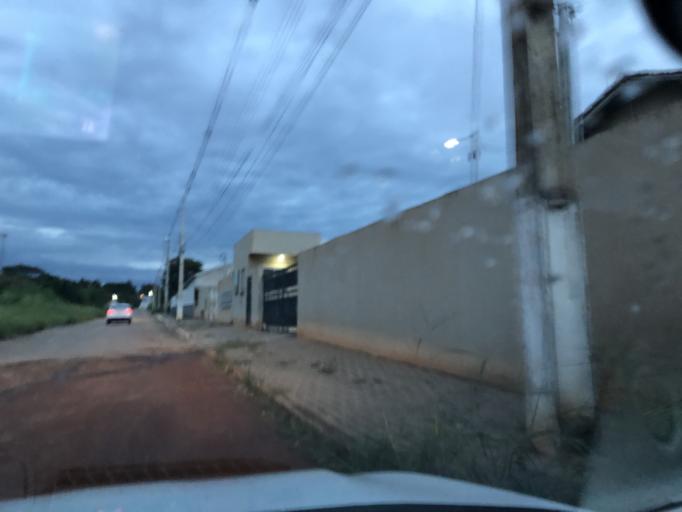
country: BR
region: Goias
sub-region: Luziania
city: Luziania
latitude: -16.1146
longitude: -47.9885
